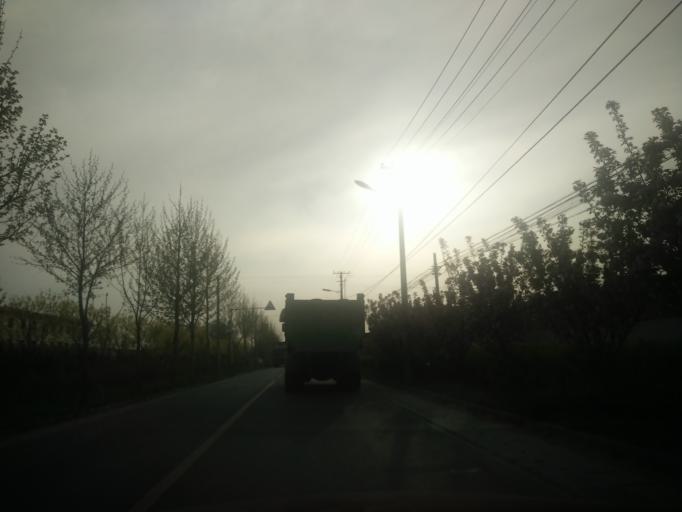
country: CN
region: Beijing
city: Qingyundian
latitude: 39.6784
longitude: 116.4581
